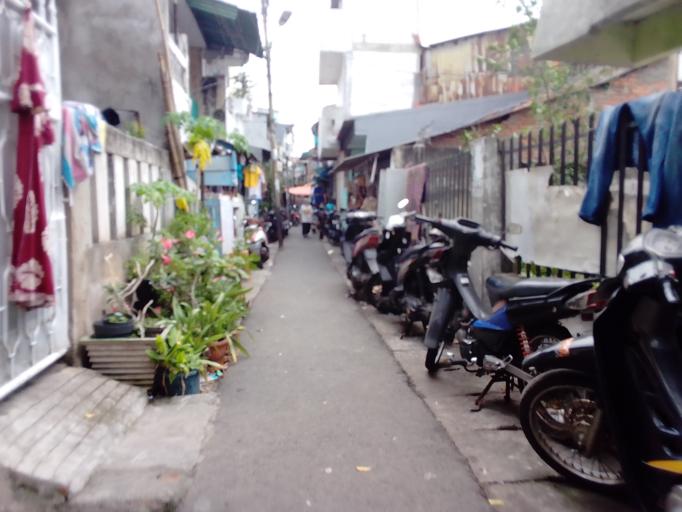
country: ID
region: Jakarta Raya
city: Jakarta
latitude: -6.1574
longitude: 106.8125
